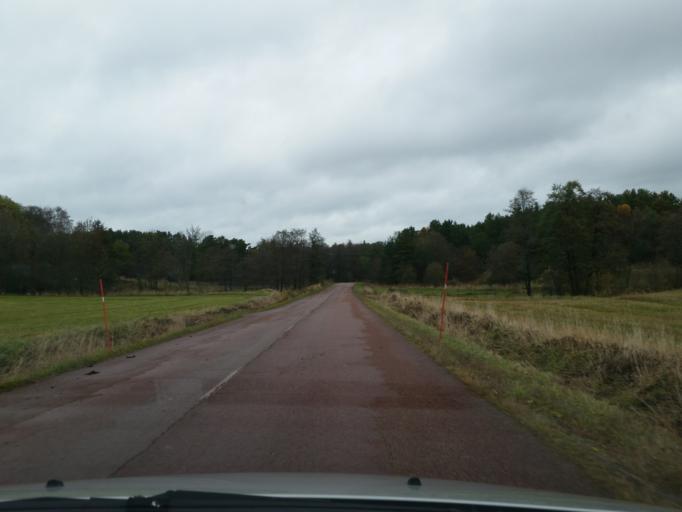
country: AX
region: Alands landsbygd
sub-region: Lumparland
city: Lumparland
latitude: 60.1300
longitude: 20.2415
